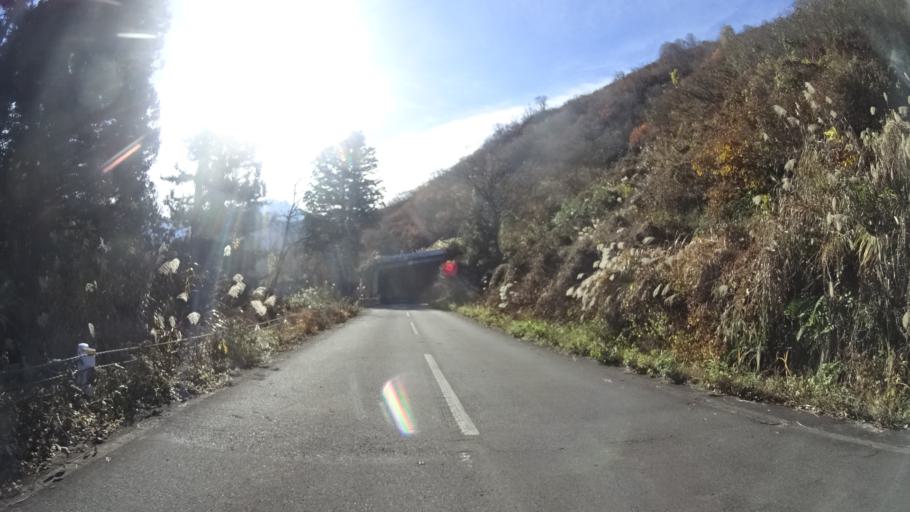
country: JP
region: Niigata
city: Muikamachi
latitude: 37.1877
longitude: 139.0816
